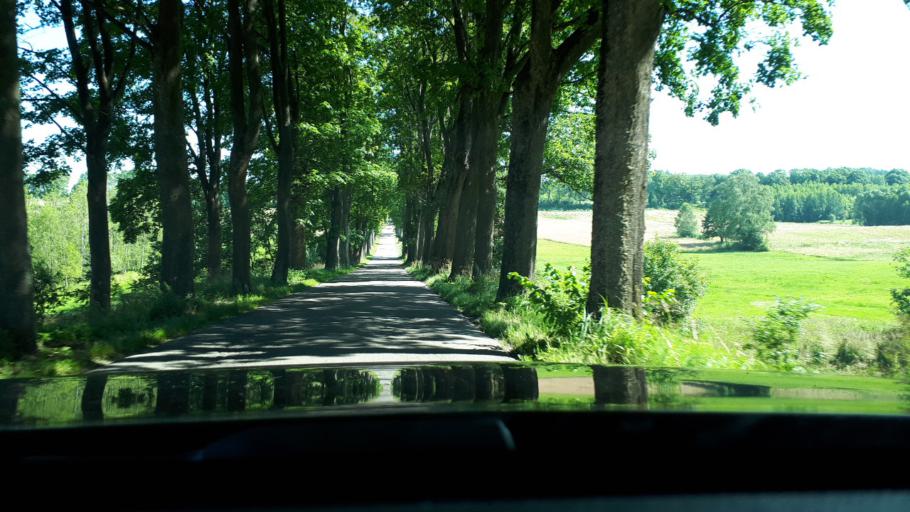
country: PL
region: Warmian-Masurian Voivodeship
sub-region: Powiat ostrodzki
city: Ostroda
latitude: 53.6823
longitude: 20.0541
